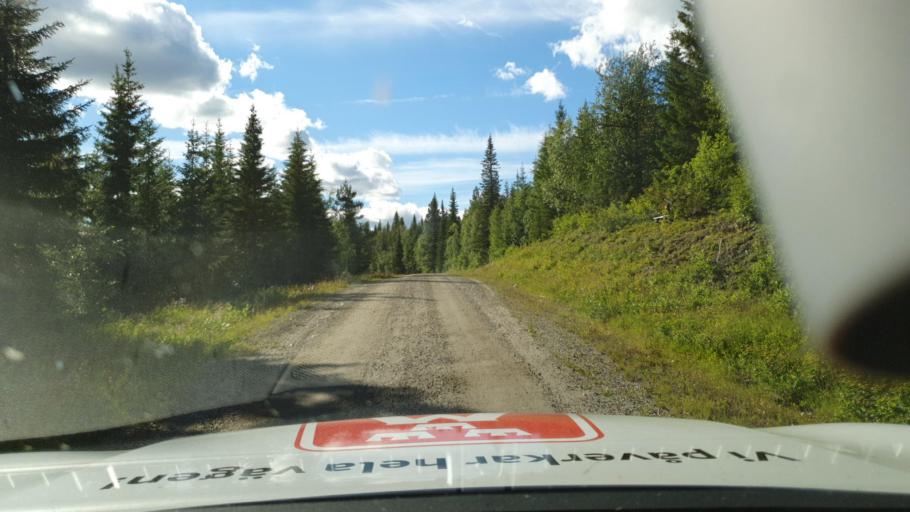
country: SE
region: Vaesterbotten
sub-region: Lycksele Kommun
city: Lycksele
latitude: 64.4038
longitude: 18.3033
